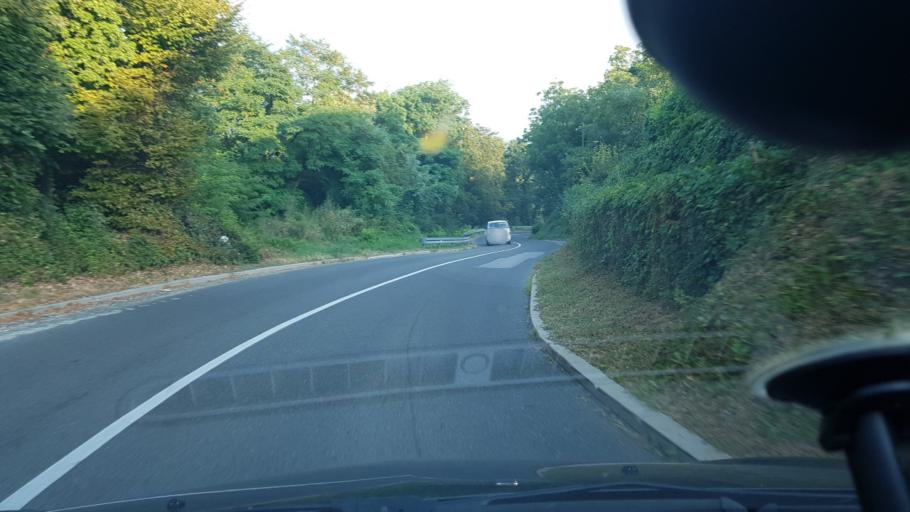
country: HR
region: Krapinsko-Zagorska
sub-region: Grad Krapina
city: Krapina
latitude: 46.1637
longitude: 15.8574
